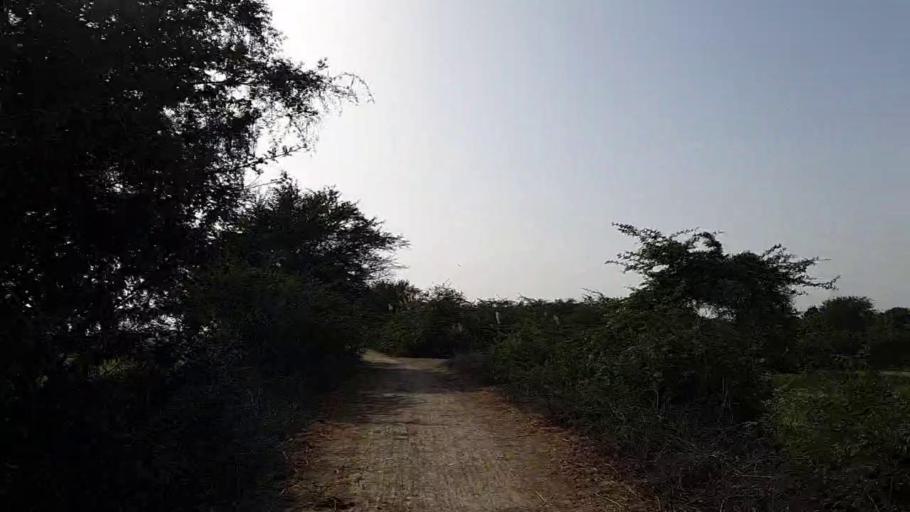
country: PK
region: Sindh
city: Jati
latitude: 24.2847
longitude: 68.1510
